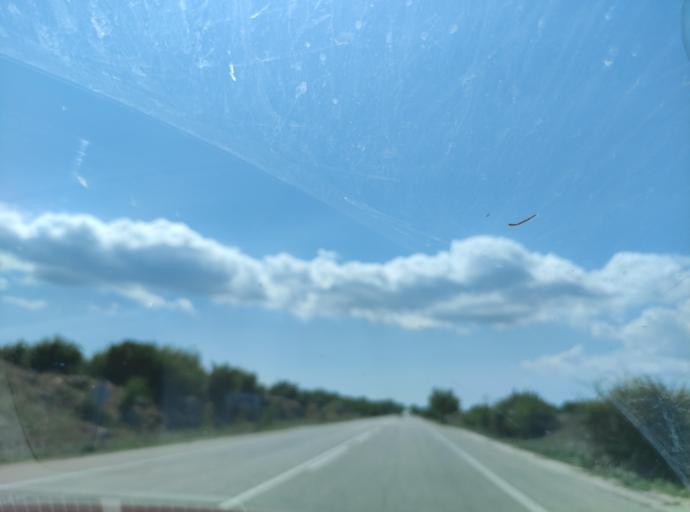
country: GR
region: East Macedonia and Thrace
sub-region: Nomos Dramas
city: Fotolivos
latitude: 40.9912
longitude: 24.0718
